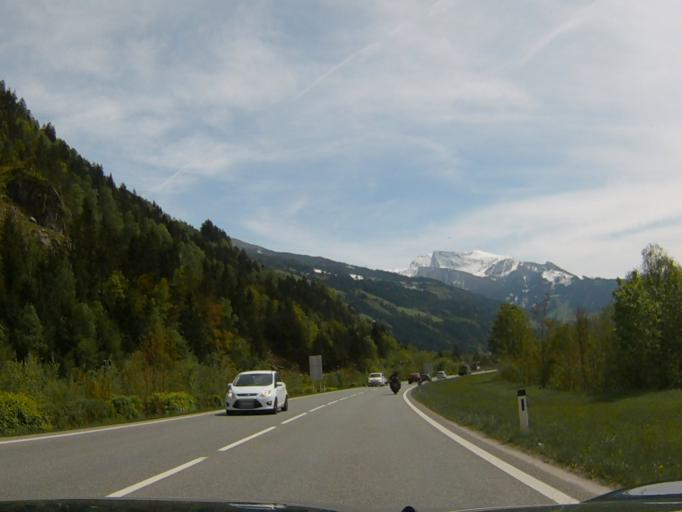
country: AT
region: Tyrol
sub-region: Politischer Bezirk Schwaz
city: Stummerberg
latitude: 47.2709
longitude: 11.9003
